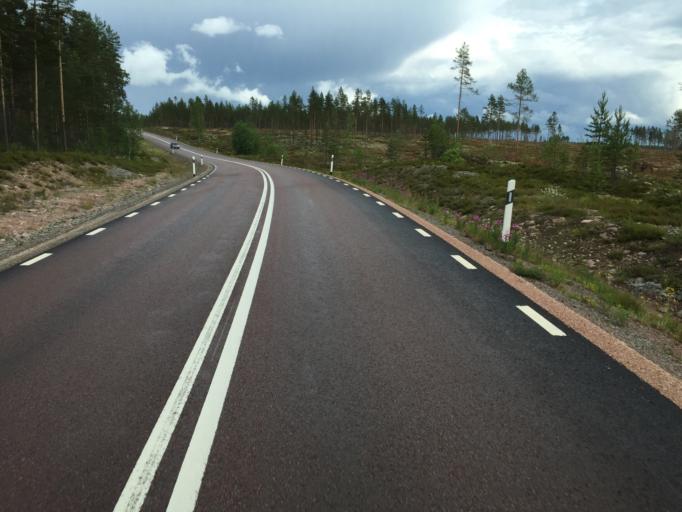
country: SE
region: Dalarna
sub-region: Malung-Saelens kommun
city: Malung
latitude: 60.8231
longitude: 13.9840
